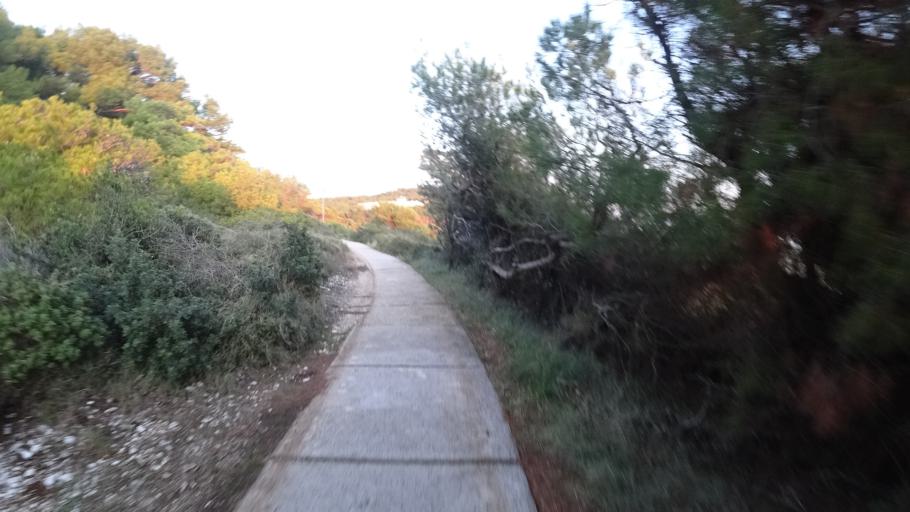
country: HR
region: Primorsko-Goranska
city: Mali Losinj
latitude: 44.5237
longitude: 14.4519
